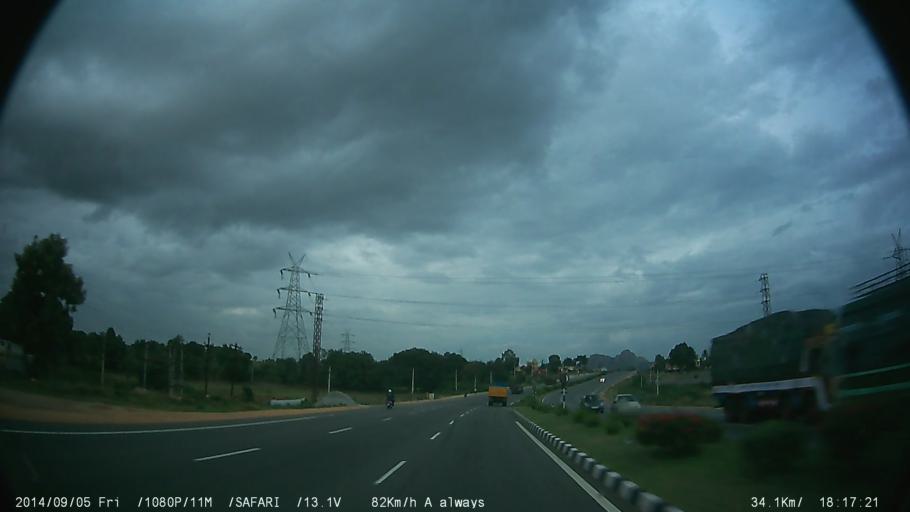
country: IN
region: Tamil Nadu
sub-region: Krishnagiri
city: Kelamangalam
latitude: 12.6714
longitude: 77.9809
